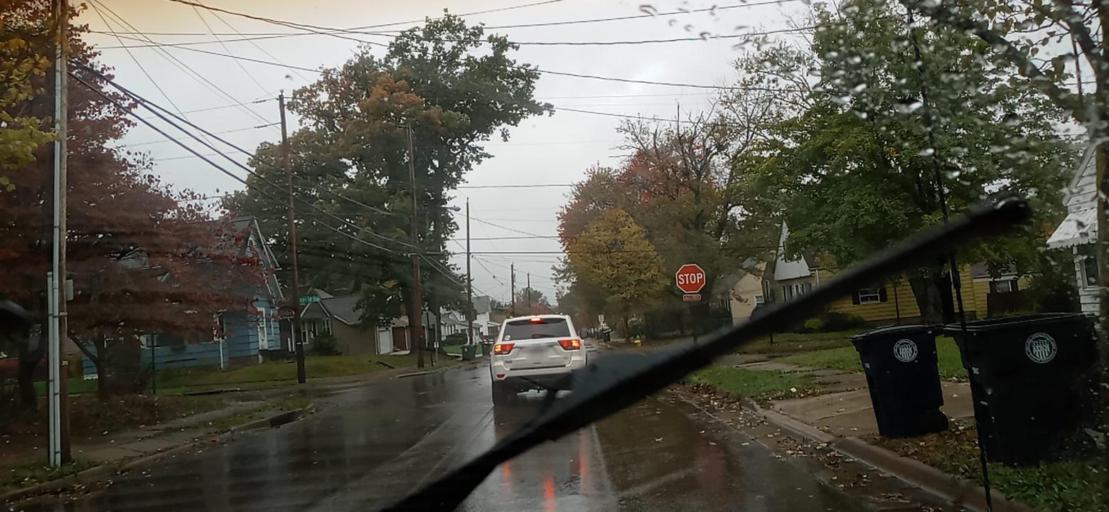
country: US
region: Ohio
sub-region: Summit County
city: Akron
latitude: 41.0572
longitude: -81.5568
